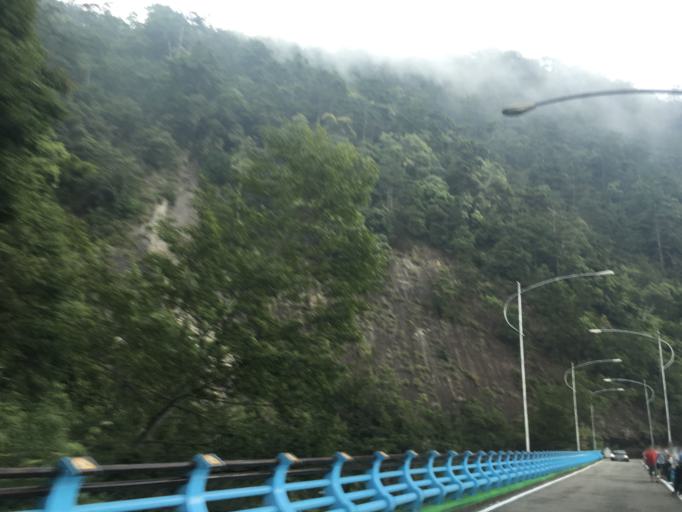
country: TW
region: Taiwan
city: Fengyuan
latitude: 24.2309
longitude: 120.9783
